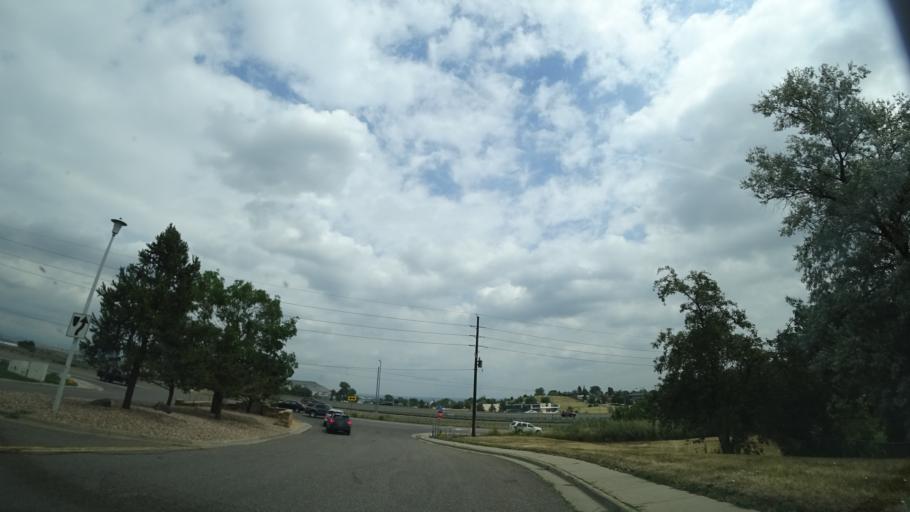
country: US
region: Colorado
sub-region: Jefferson County
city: West Pleasant View
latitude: 39.7244
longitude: -105.1593
